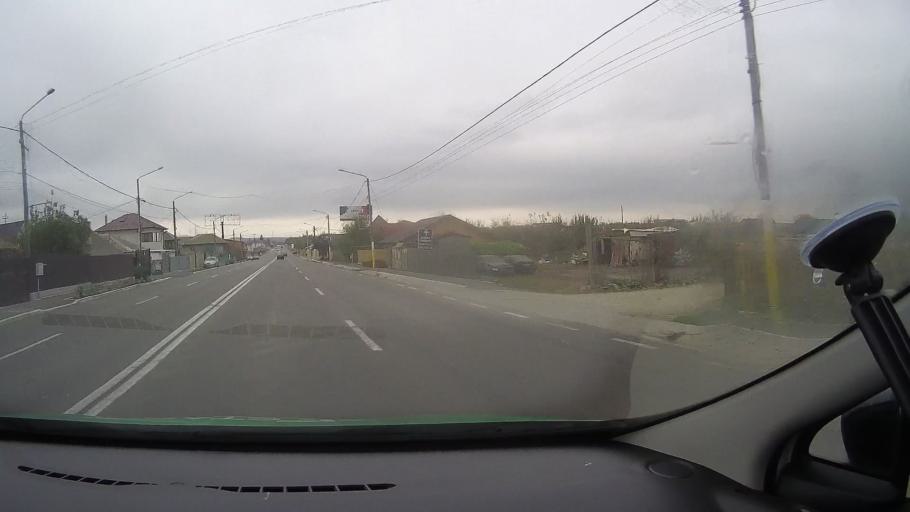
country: RO
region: Constanta
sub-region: Comuna Valu lui Traian
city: Valu lui Traian
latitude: 44.1684
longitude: 28.4475
